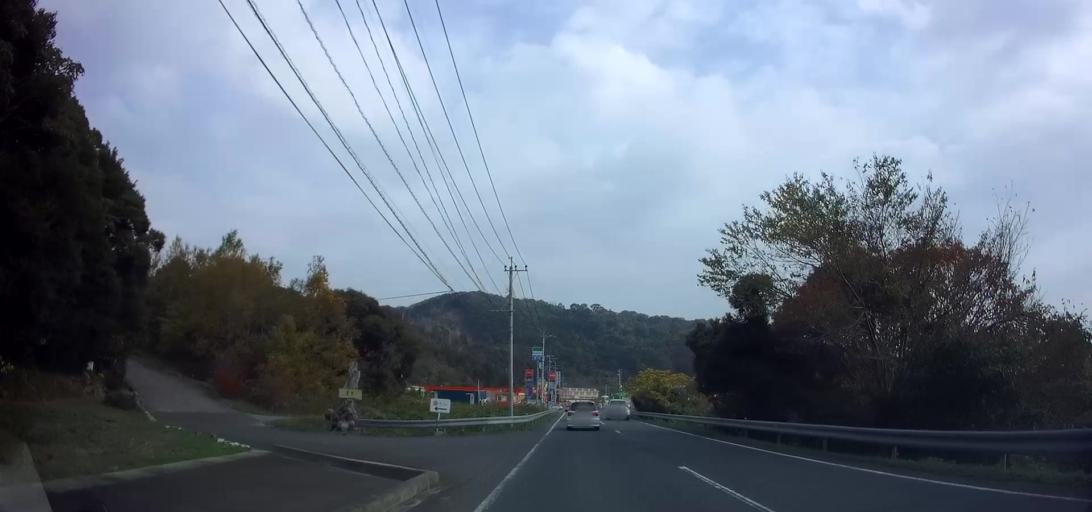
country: JP
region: Nagasaki
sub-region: Isahaya-shi
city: Isahaya
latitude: 32.7933
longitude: 130.1136
